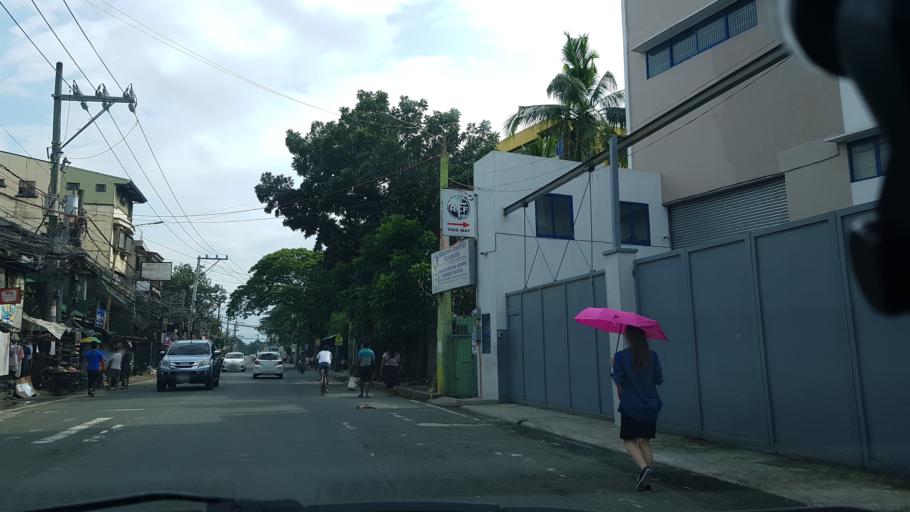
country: PH
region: Metro Manila
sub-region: Pasig
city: Pasig City
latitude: 14.5893
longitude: 121.0893
